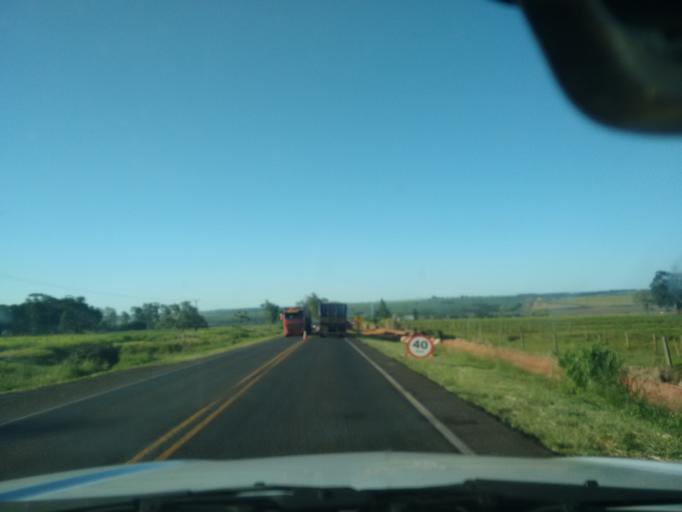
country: BR
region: Mato Grosso do Sul
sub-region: Eldorado
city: Eldorado
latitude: -23.8525
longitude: -54.3366
